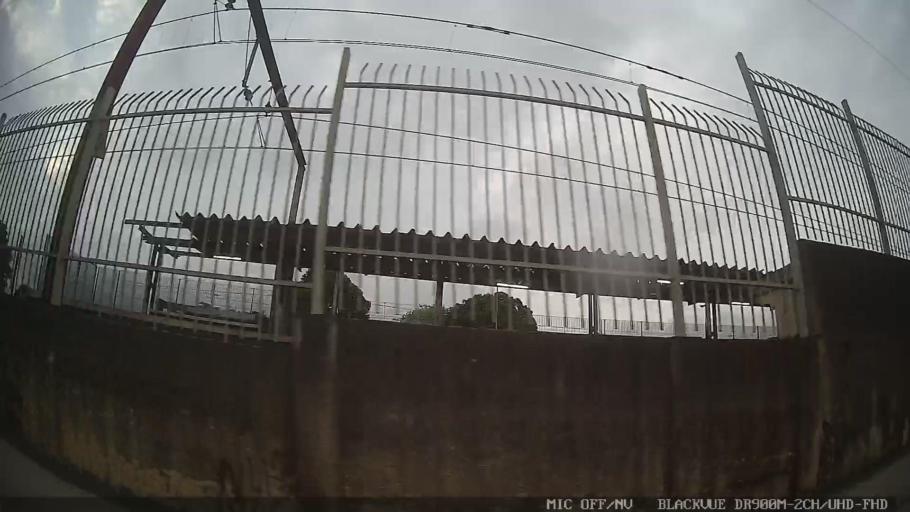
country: BR
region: Sao Paulo
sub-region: Mogi das Cruzes
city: Mogi das Cruzes
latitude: -23.5224
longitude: -46.1990
